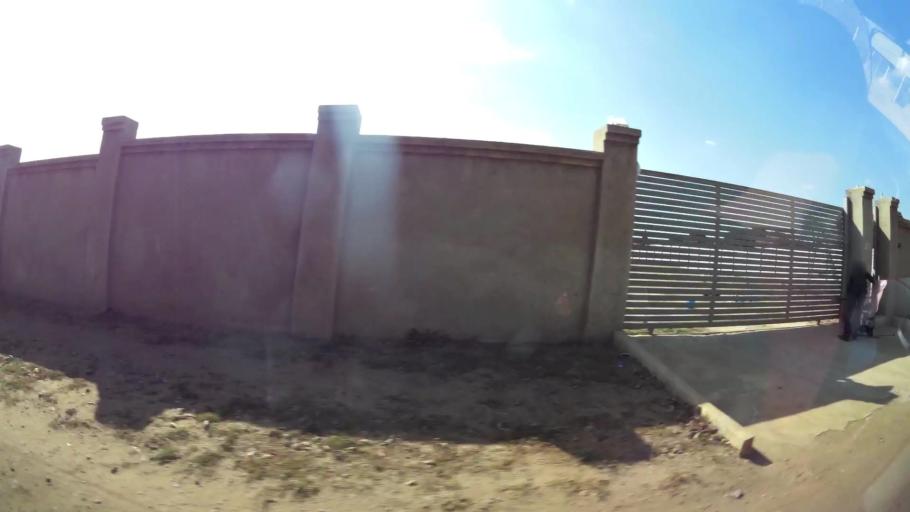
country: ZA
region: Gauteng
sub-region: Ekurhuleni Metropolitan Municipality
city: Benoni
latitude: -26.0818
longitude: 28.3399
